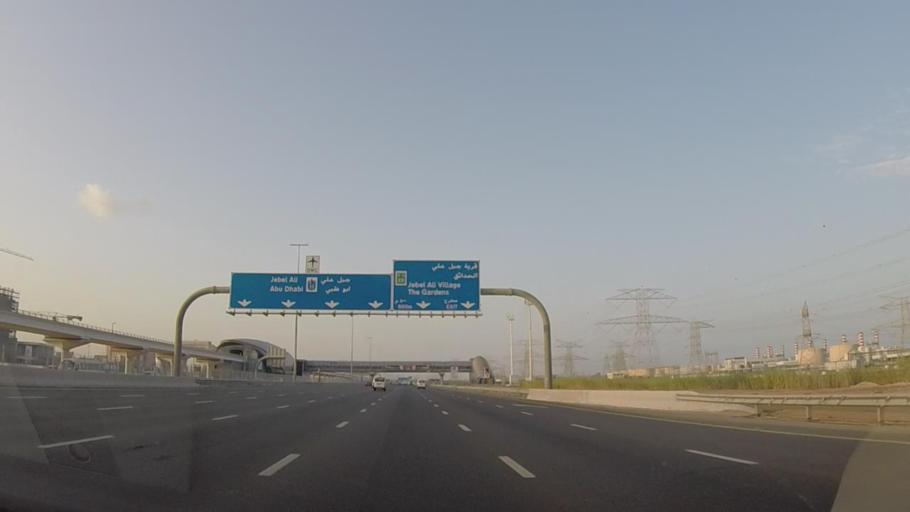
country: AE
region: Dubai
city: Dubai
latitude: 25.0491
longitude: 55.1187
